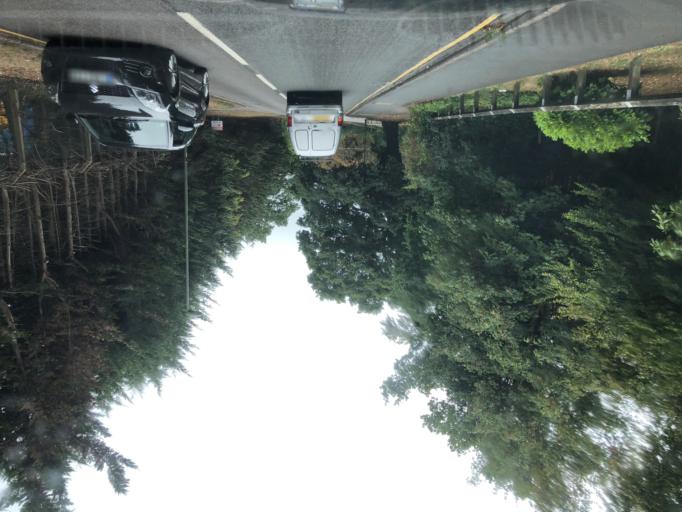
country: GB
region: England
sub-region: Surrey
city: Frimley
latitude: 51.2989
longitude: -0.7288
